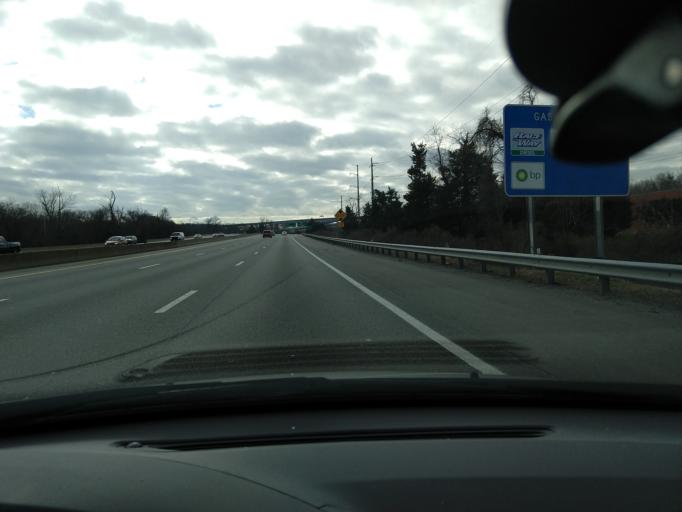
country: US
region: Virginia
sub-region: Chesterfield County
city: Bensley
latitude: 37.4518
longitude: -77.4242
